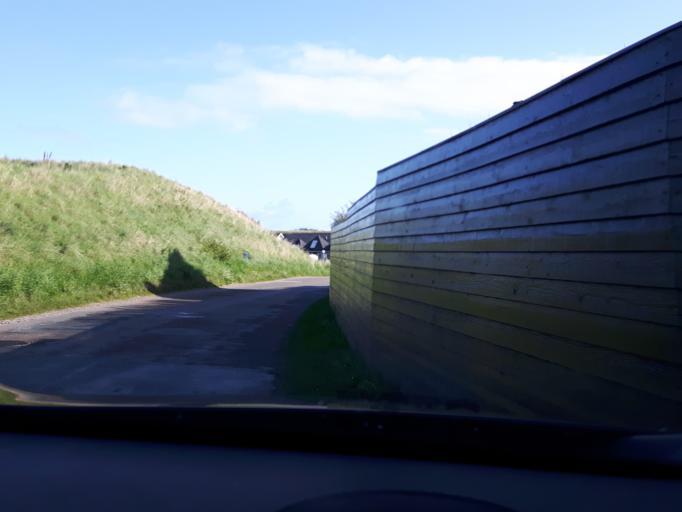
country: DK
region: North Denmark
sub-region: Hjorring Kommune
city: Hjorring
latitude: 57.4658
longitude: 9.7963
